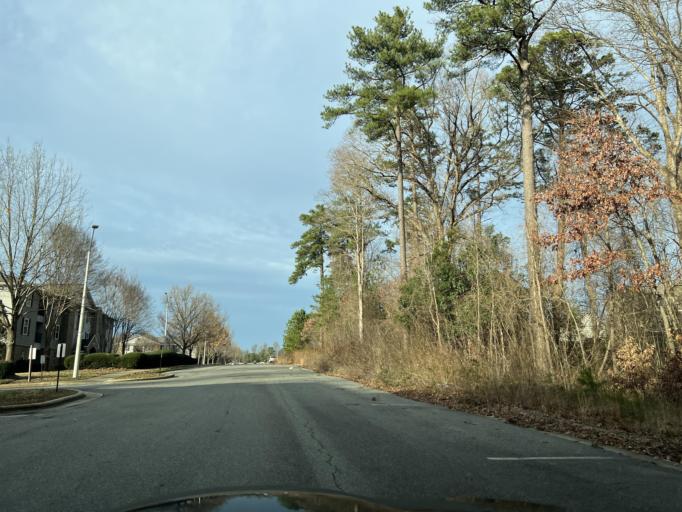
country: US
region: North Carolina
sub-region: Wake County
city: Cary
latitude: 35.7823
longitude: -78.7313
